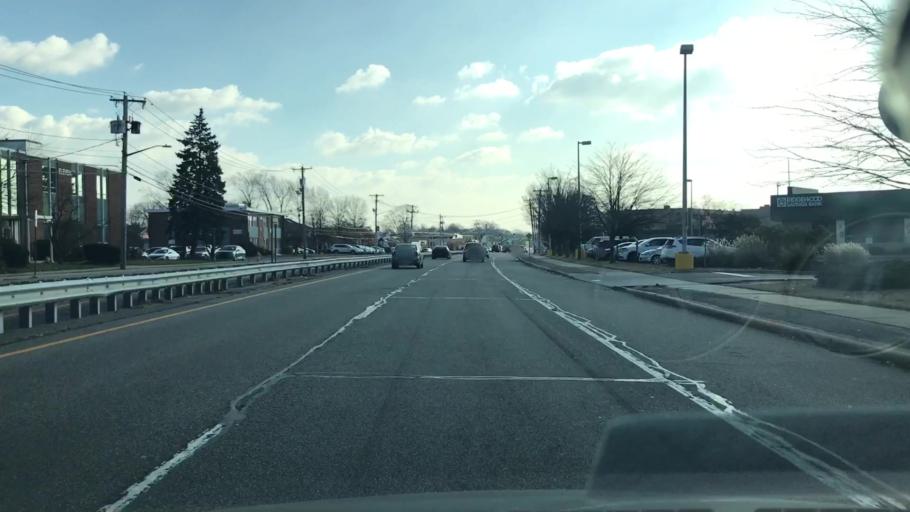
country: US
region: New York
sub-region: Suffolk County
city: West Babylon
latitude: 40.7052
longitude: -73.3464
